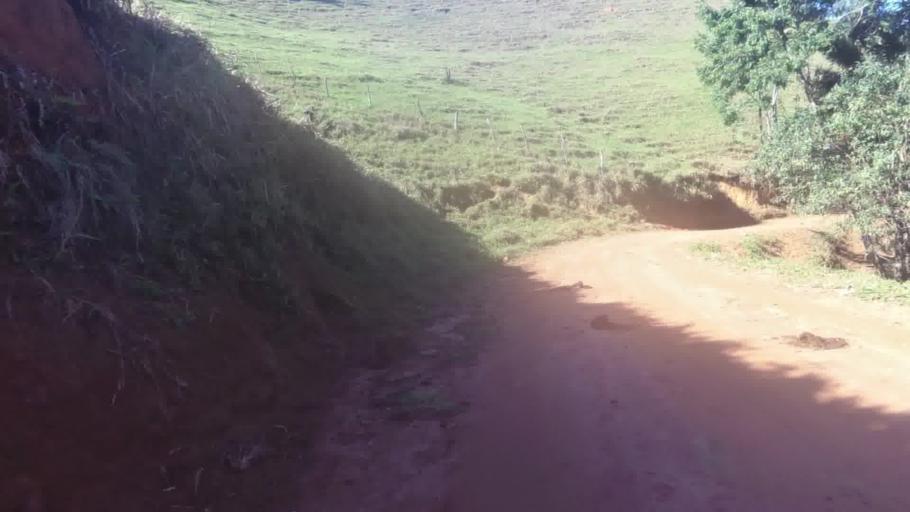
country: BR
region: Espirito Santo
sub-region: Alfredo Chaves
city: Alfredo Chaves
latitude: -20.6728
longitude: -40.7816
